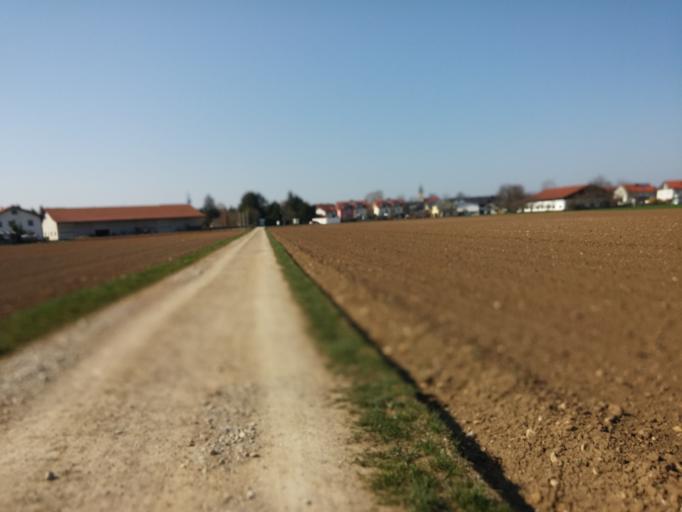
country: DE
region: Bavaria
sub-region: Upper Bavaria
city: Haar
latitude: 48.1269
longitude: 11.7188
